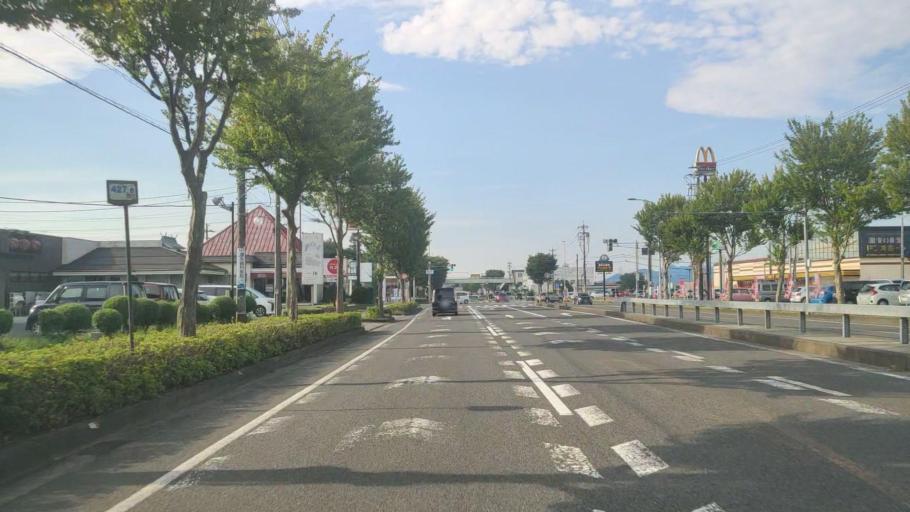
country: JP
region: Fukui
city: Takefu
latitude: 35.9073
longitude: 136.1921
